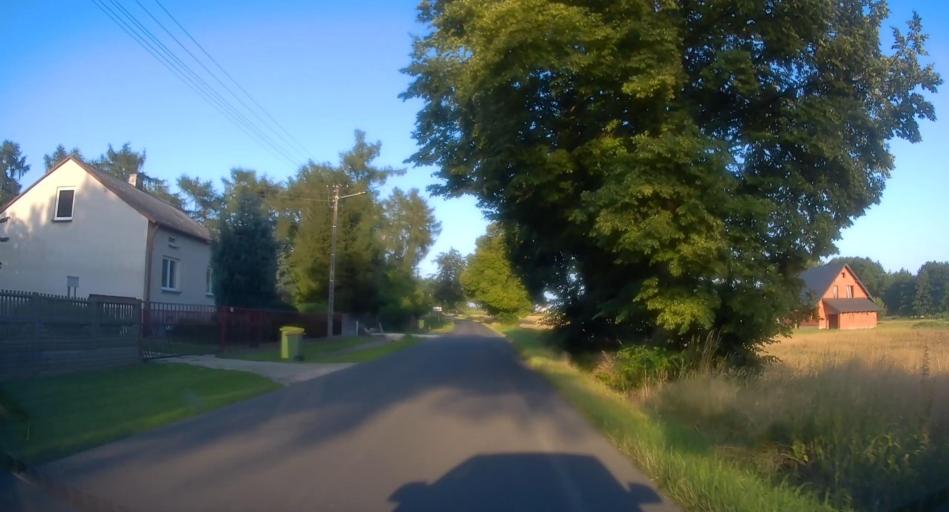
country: PL
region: Lodz Voivodeship
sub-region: Powiat skierniewicki
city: Kaweczyn Nowy
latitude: 51.8841
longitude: 20.2583
